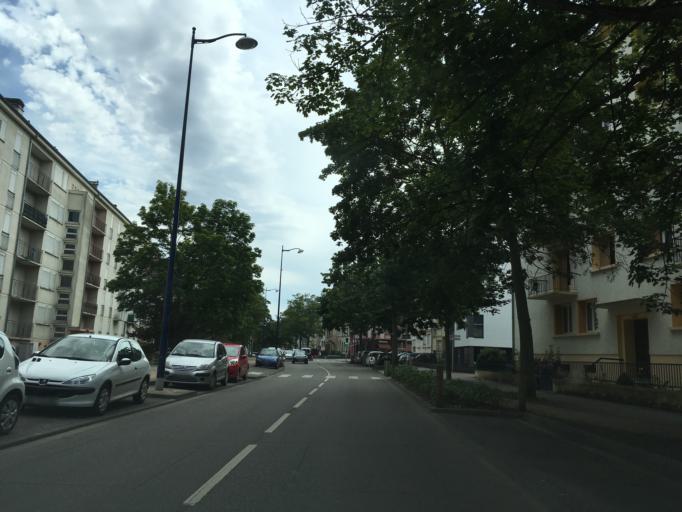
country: FR
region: Lorraine
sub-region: Departement de la Moselle
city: Metz
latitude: 49.1010
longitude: 6.1776
